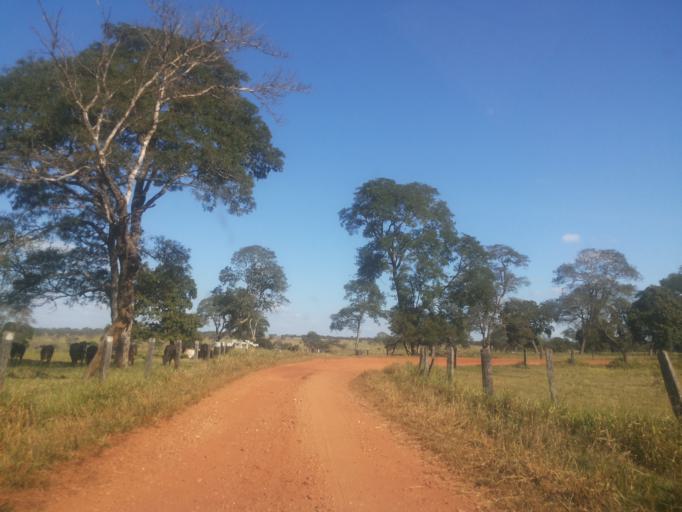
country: BR
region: Minas Gerais
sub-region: Santa Vitoria
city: Santa Vitoria
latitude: -19.0116
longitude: -50.4010
